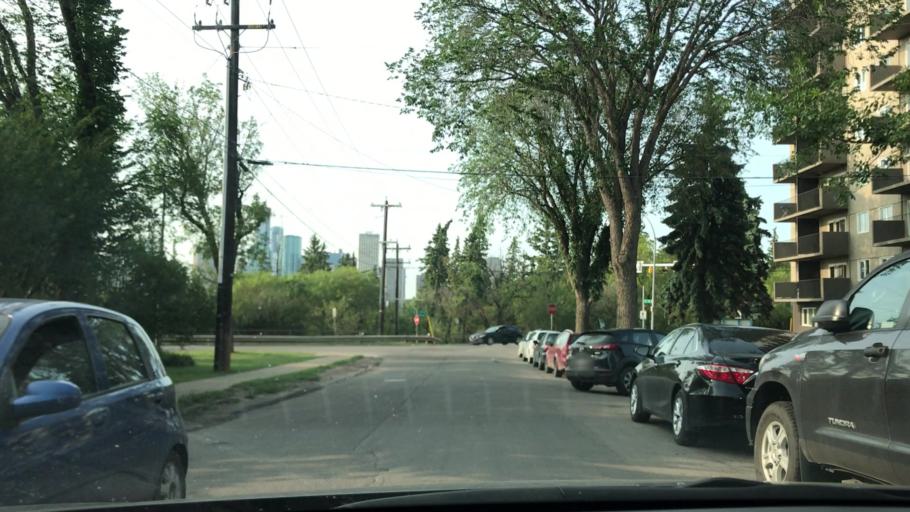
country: CA
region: Alberta
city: Edmonton
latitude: 53.5257
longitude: -113.4887
